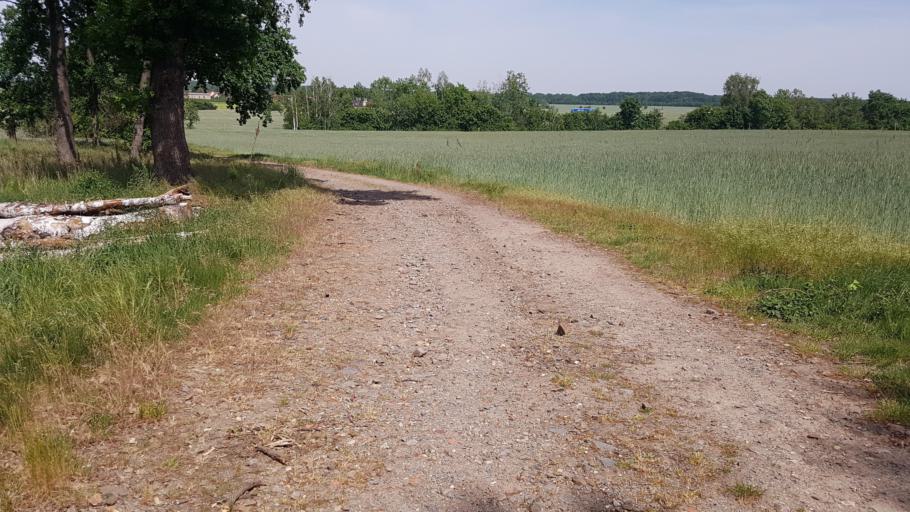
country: DE
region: Brandenburg
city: Grosskmehlen
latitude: 51.3758
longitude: 13.7088
